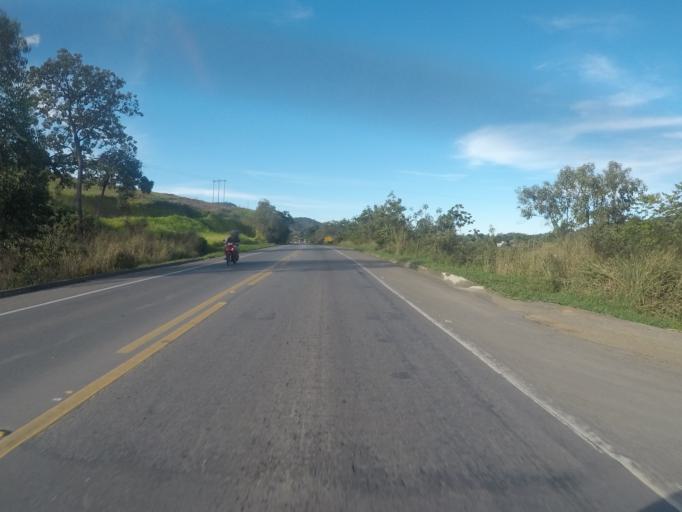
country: BR
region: Espirito Santo
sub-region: Ibiracu
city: Ibiracu
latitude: -19.8663
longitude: -40.3981
